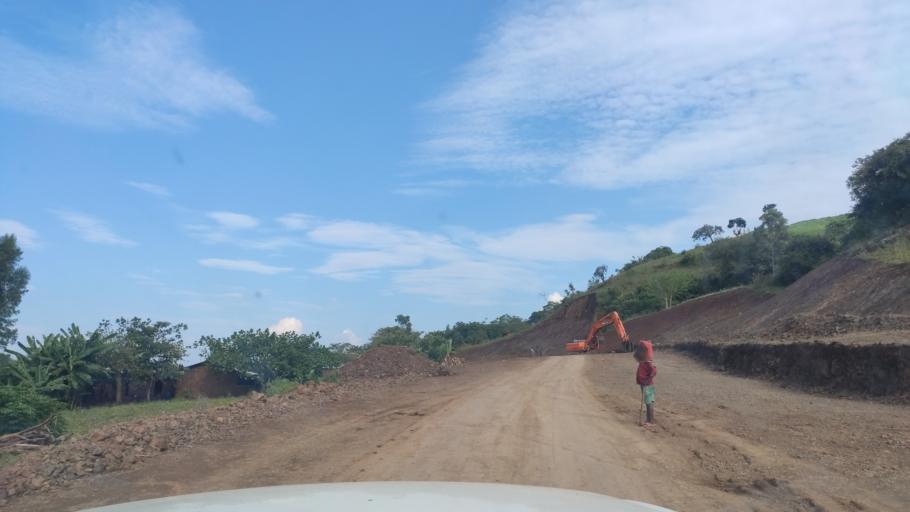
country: ET
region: Southern Nations, Nationalities, and People's Region
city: Arba Minch'
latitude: 6.4209
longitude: 37.3553
